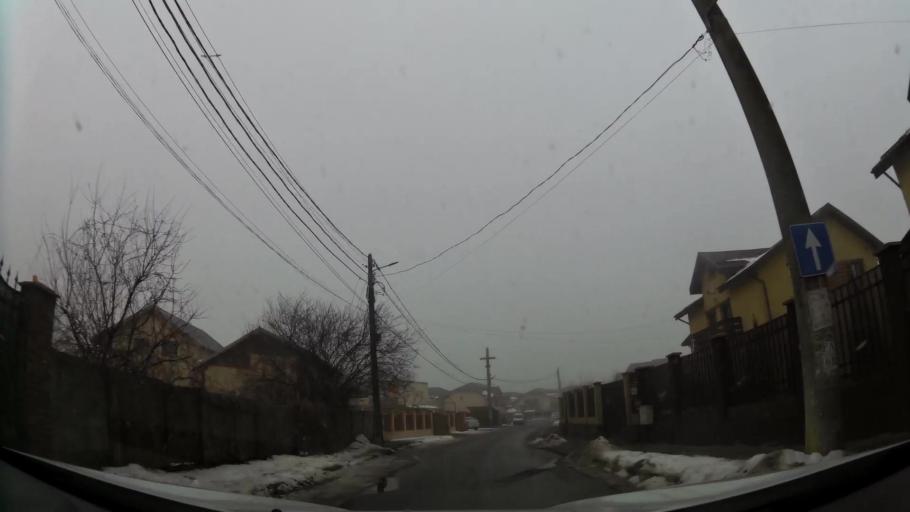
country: RO
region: Ilfov
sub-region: Comuna Chiajna
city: Chiajna
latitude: 44.4565
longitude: 25.9735
